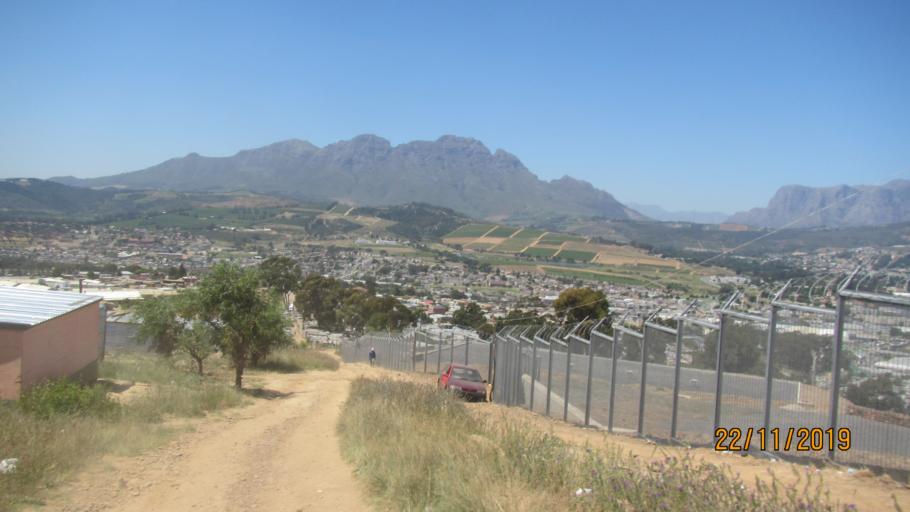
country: ZA
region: Western Cape
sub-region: Cape Winelands District Municipality
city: Stellenbosch
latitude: -33.9246
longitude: 18.8398
